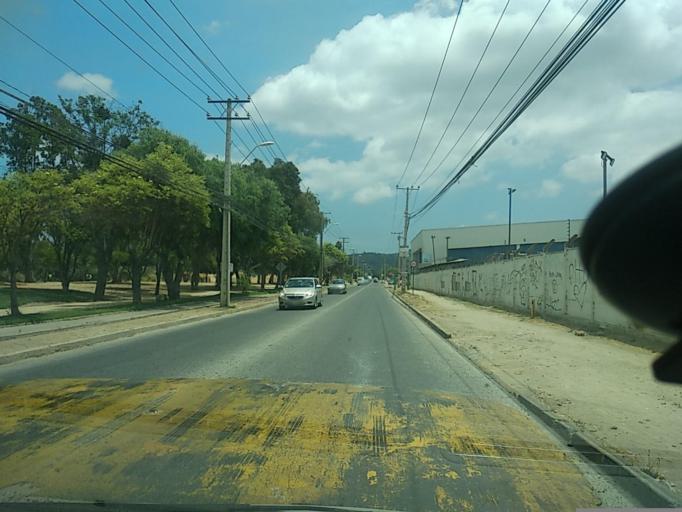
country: CL
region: Valparaiso
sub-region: Provincia de Marga Marga
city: Quilpue
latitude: -33.0408
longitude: -71.4161
